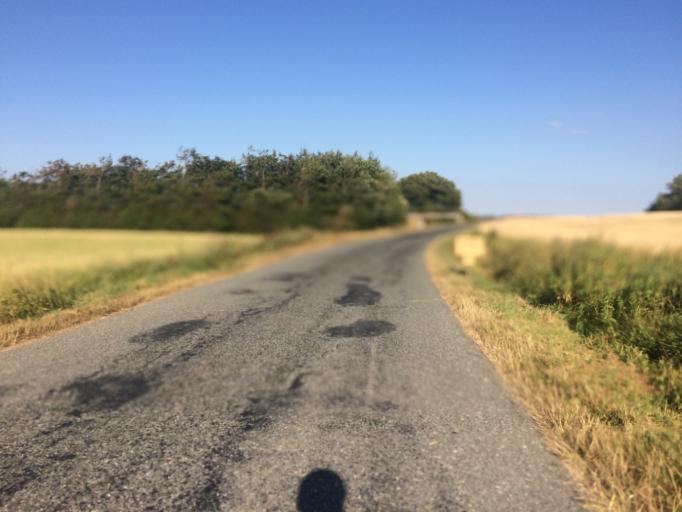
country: DK
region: Central Jutland
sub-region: Holstebro Kommune
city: Vinderup
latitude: 56.5869
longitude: 8.7741
